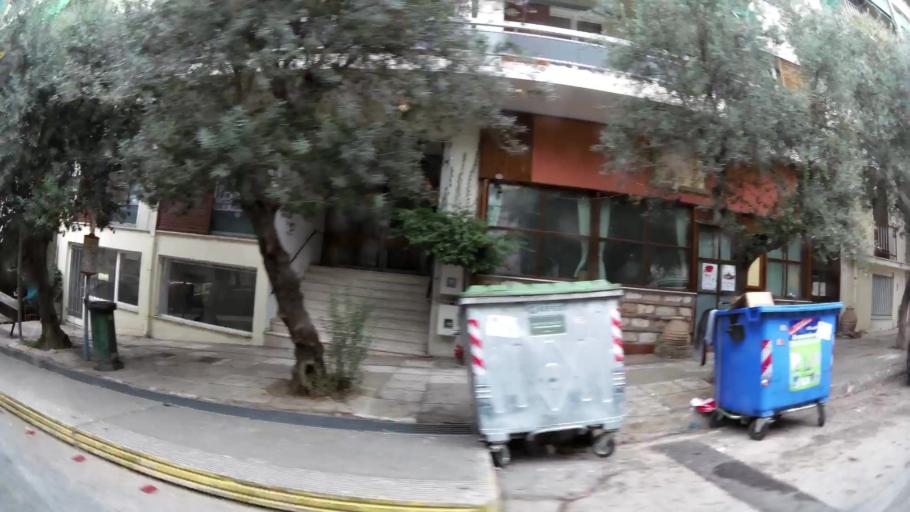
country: GR
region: Attica
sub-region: Nomarchia Athinas
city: Vyronas
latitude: 37.9654
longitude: 23.7436
